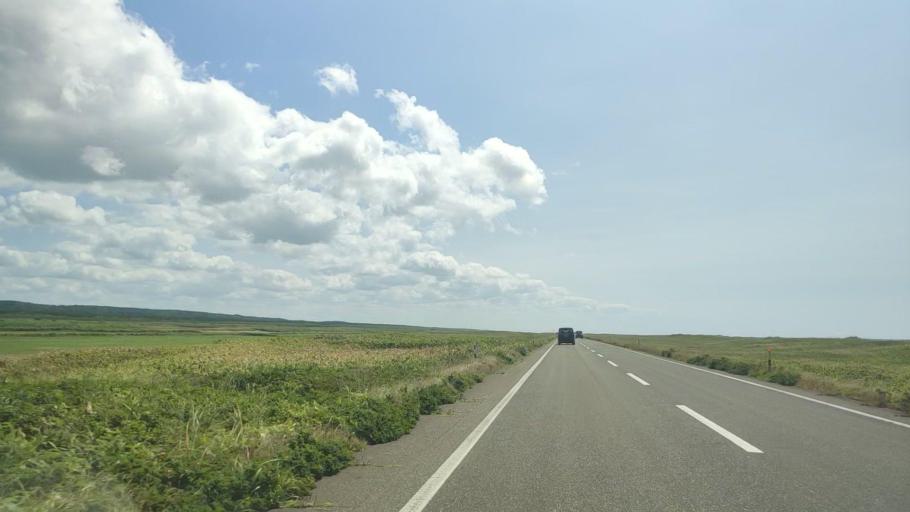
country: JP
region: Hokkaido
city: Wakkanai
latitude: 45.1209
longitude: 141.6090
